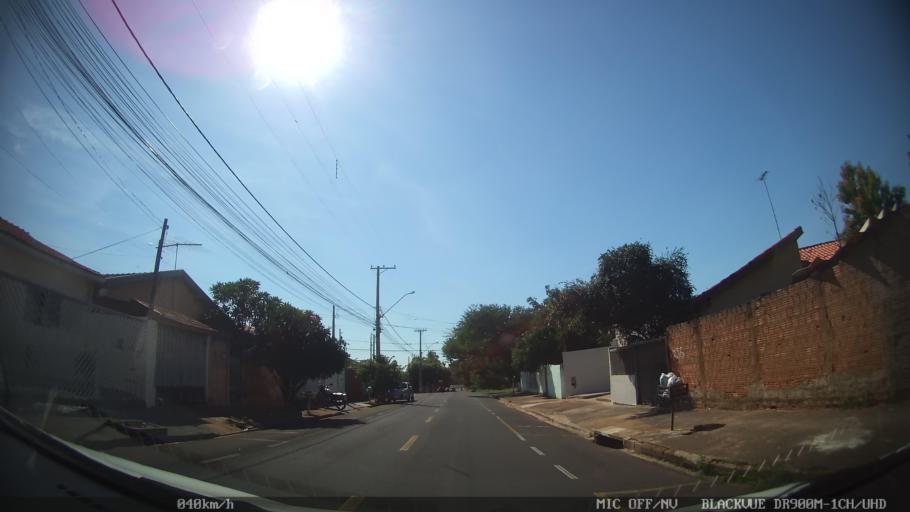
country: BR
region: Sao Paulo
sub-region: Sao Jose Do Rio Preto
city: Sao Jose do Rio Preto
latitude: -20.7726
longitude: -49.4176
